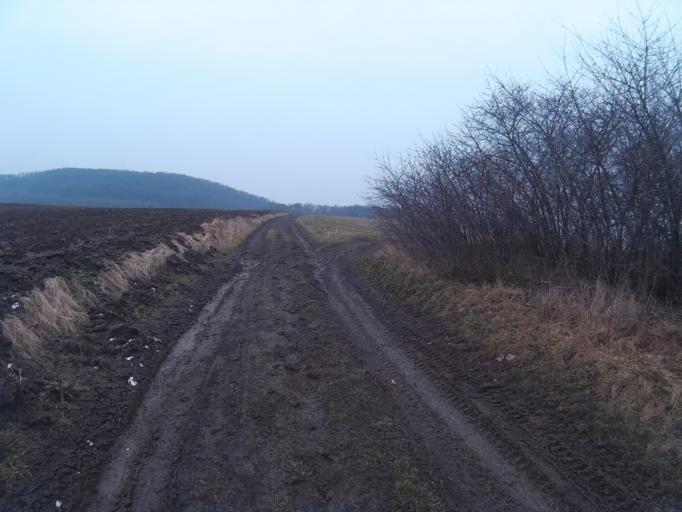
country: HU
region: Komarom-Esztergom
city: Tarjan
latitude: 47.6017
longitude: 18.5142
